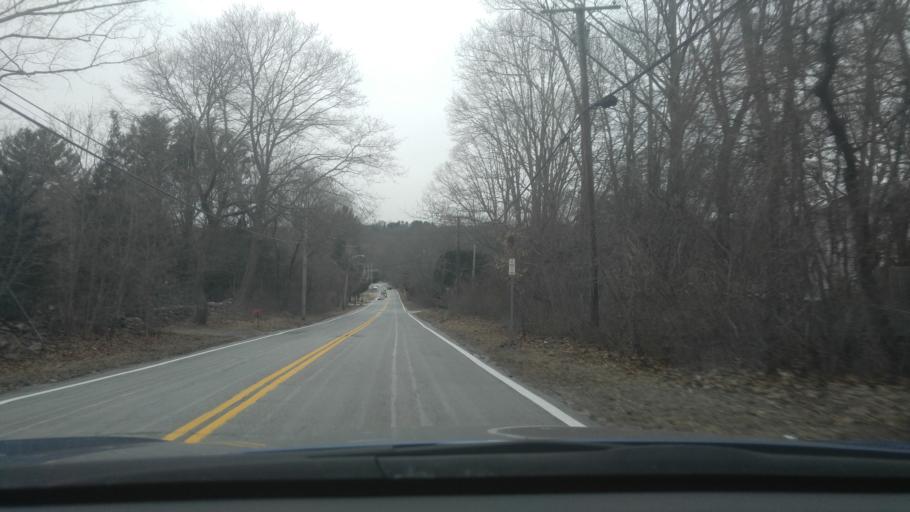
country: US
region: Rhode Island
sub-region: Washington County
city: Narragansett Pier
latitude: 41.4920
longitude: -71.4409
